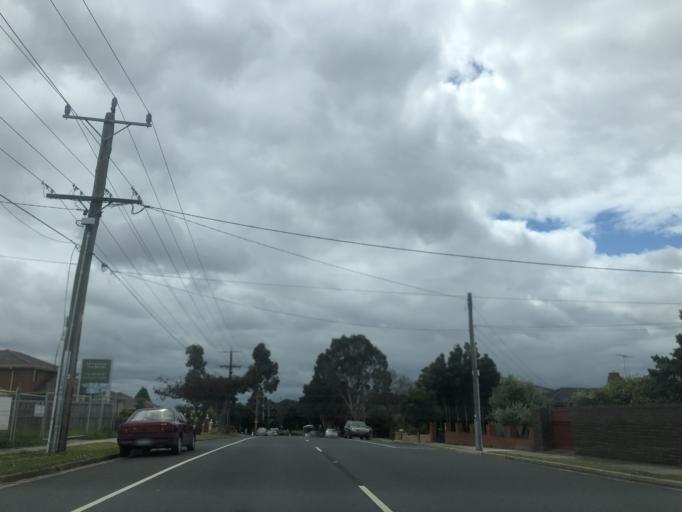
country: AU
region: Victoria
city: Clayton
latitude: -37.9220
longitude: 145.1085
